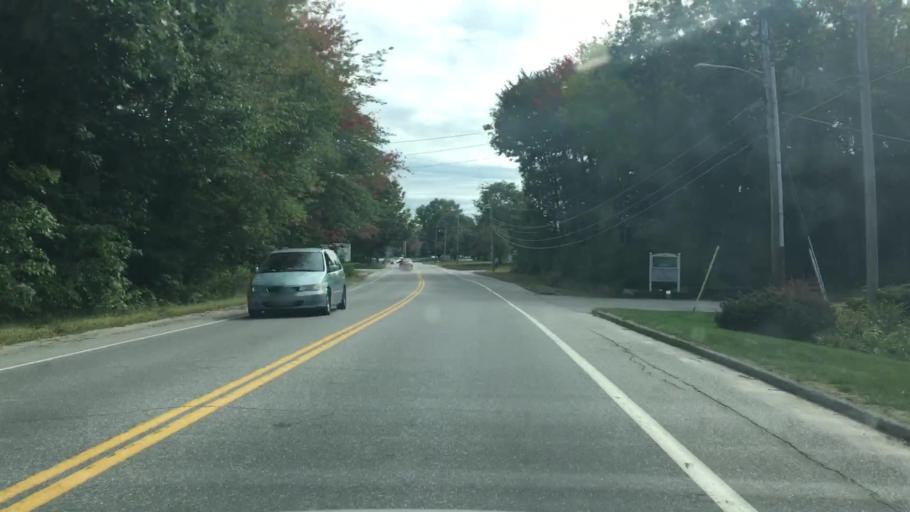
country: US
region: Maine
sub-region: Cumberland County
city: Brunswick
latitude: 43.9005
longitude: -69.9794
